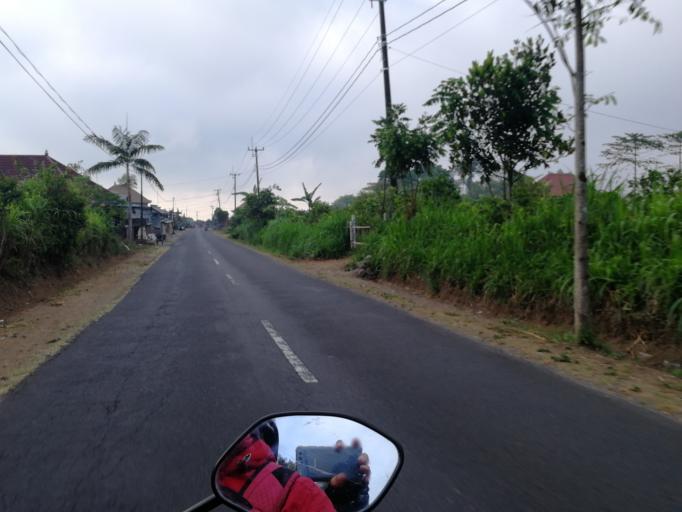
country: ID
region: Bali
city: Banjar Ambengan
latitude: -8.2263
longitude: 115.2453
